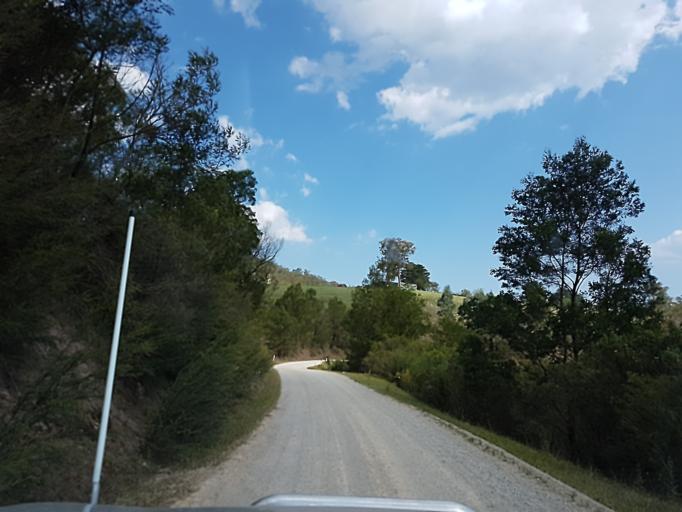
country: AU
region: Victoria
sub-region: East Gippsland
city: Lakes Entrance
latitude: -37.4857
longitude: 148.2383
